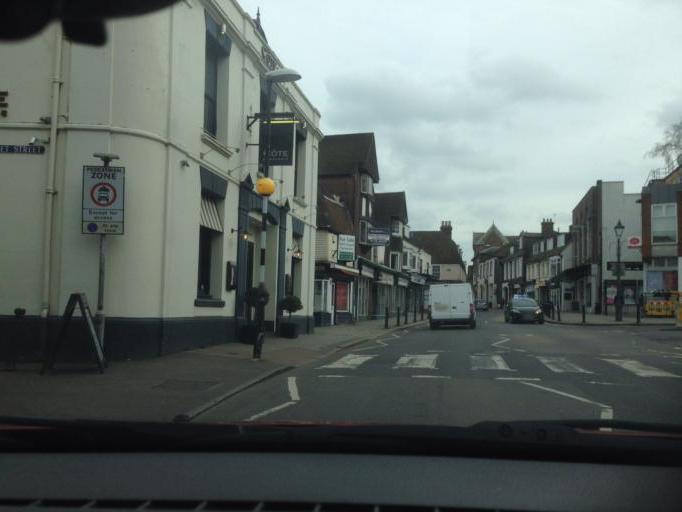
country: GB
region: England
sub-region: Kent
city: Sevenoaks
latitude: 51.2707
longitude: 0.1918
